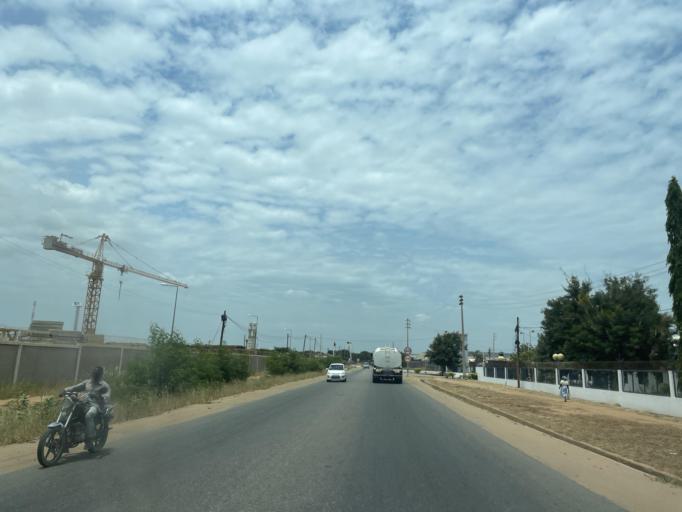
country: AO
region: Luanda
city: Luanda
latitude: -8.9315
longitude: 13.3935
